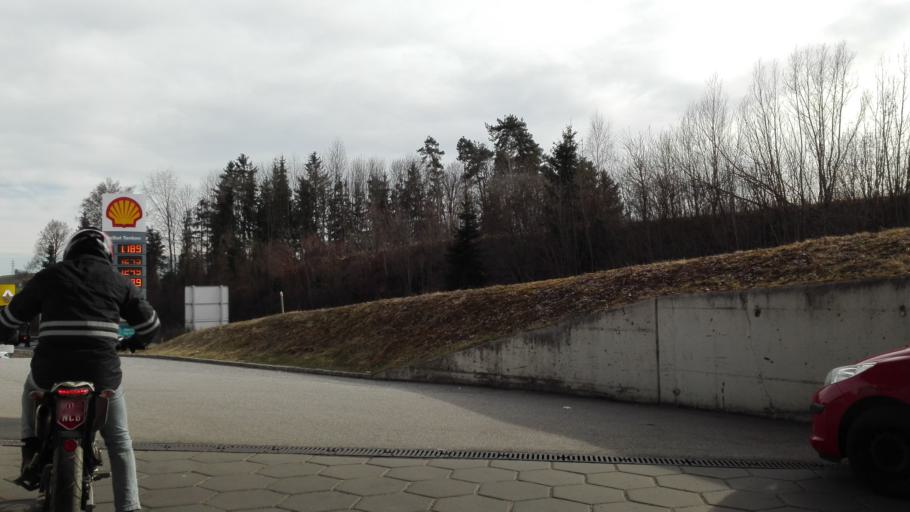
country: AT
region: Upper Austria
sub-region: Politischer Bezirk Rohrbach
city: Schlaegl
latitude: 48.5651
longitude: 13.9852
